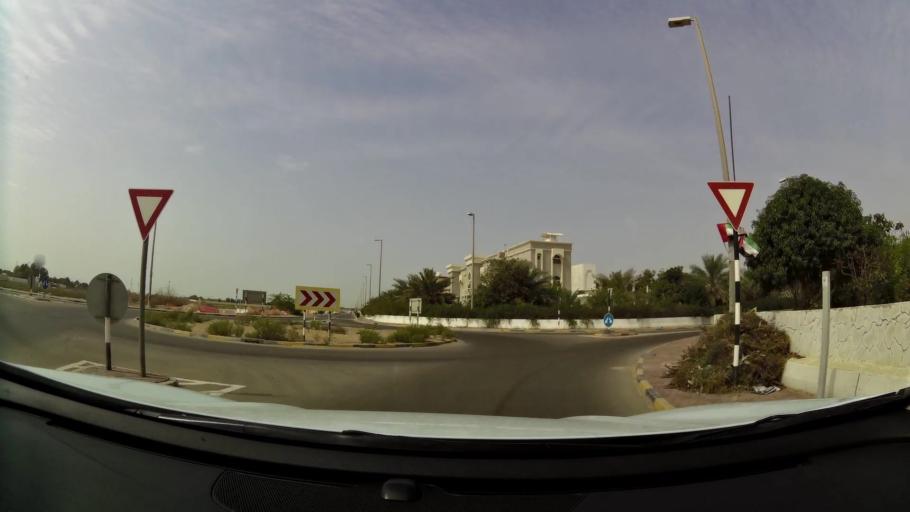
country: AE
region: Abu Dhabi
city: Abu Dhabi
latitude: 24.5416
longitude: 54.6660
